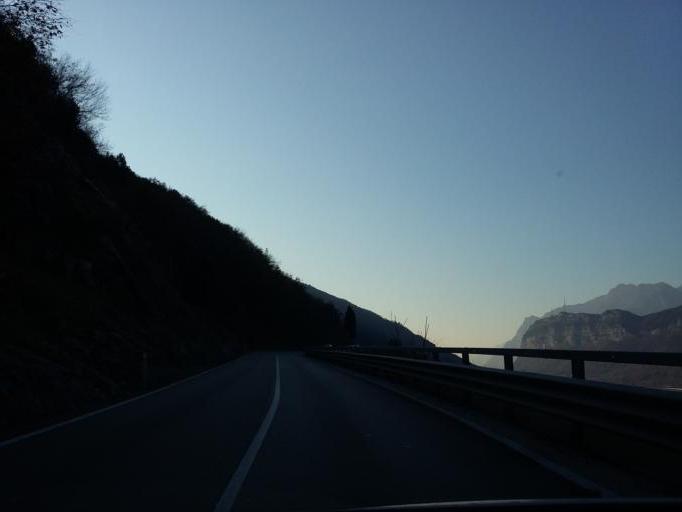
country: IT
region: Trentino-Alto Adige
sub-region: Provincia di Trento
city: Bolognano-Vignole
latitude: 45.9057
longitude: 10.9020
